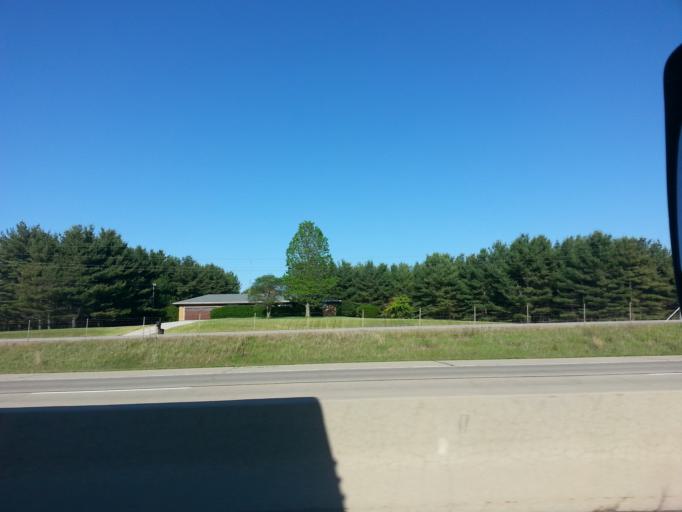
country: US
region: Illinois
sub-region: McLean County
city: Hudson
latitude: 40.6582
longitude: -89.0048
